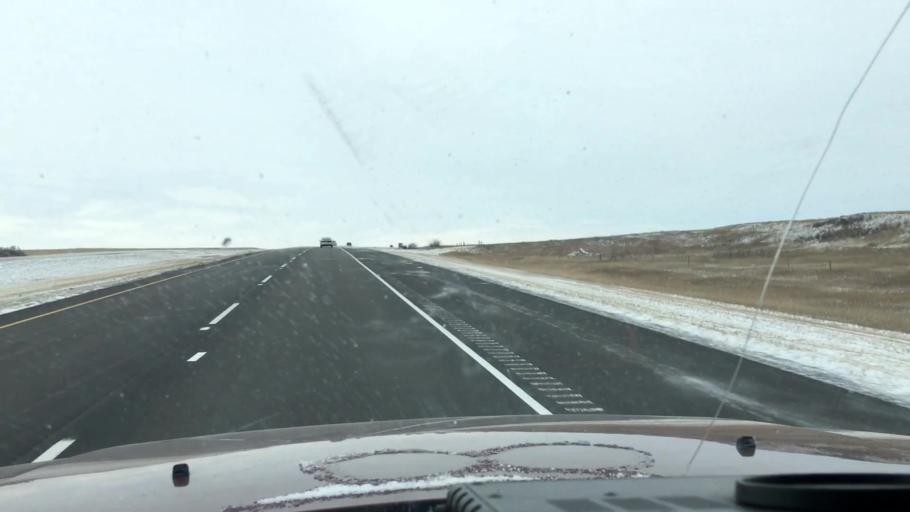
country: CA
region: Saskatchewan
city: Saskatoon
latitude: 51.7225
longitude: -106.4711
